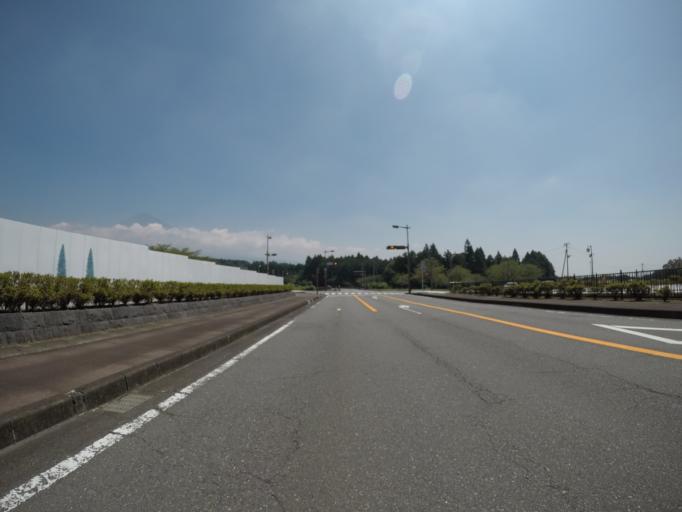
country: JP
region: Shizuoka
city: Fujinomiya
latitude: 35.2761
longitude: 138.5859
